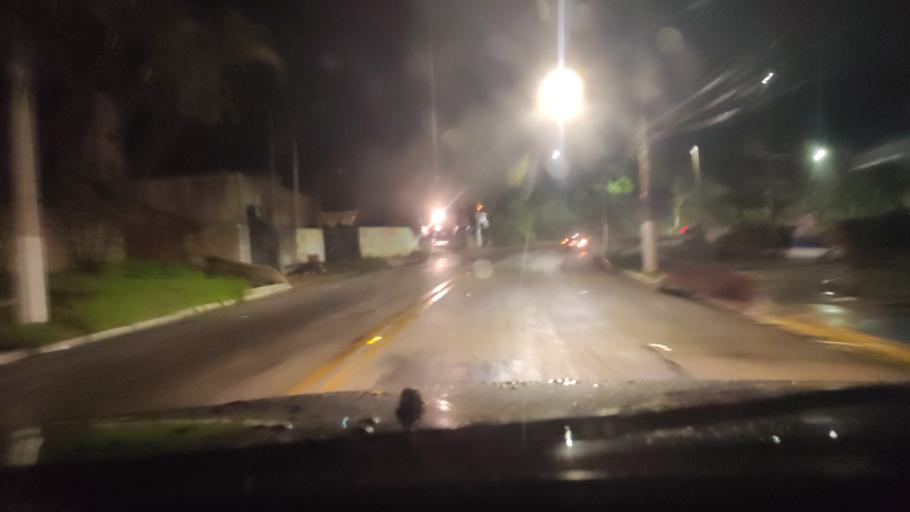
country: BR
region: Sao Paulo
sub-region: Sao Sebastiao
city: Sao Sebastiao
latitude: -23.7501
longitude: -45.4118
